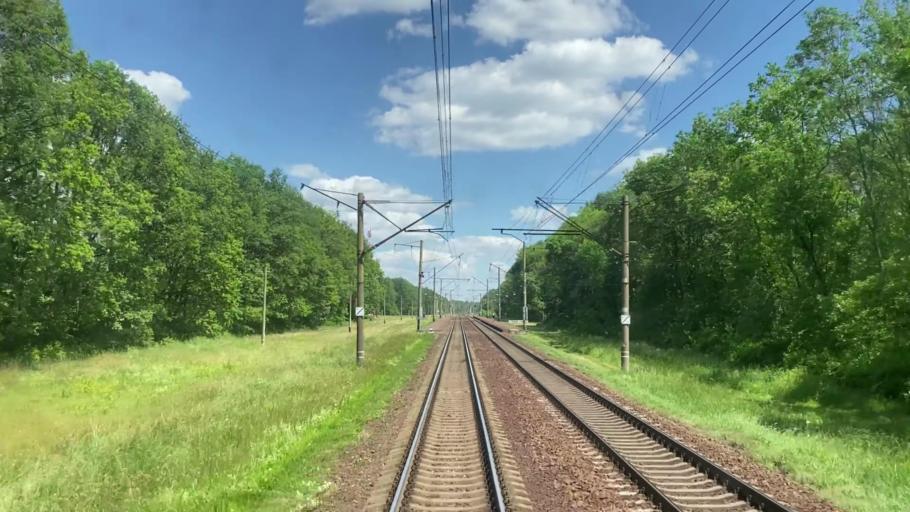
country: BY
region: Brest
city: Pruzhany
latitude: 52.4971
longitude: 24.6087
